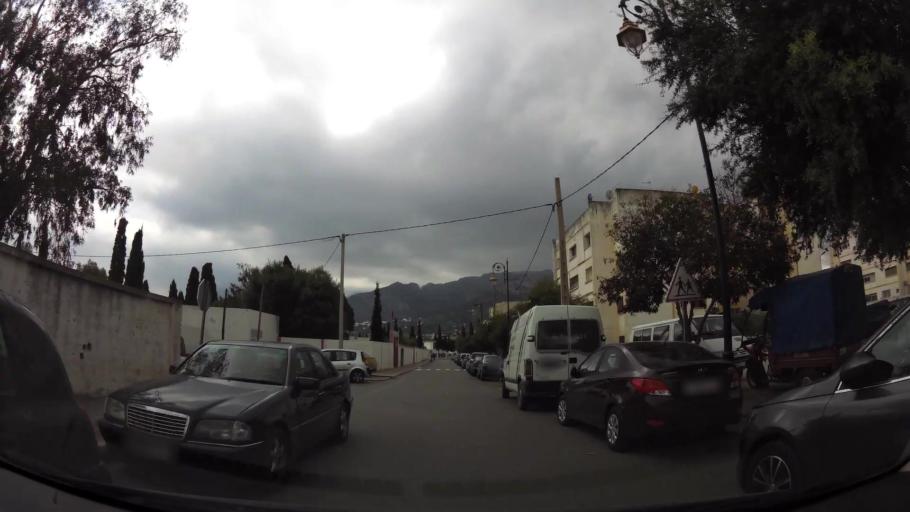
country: MA
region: Tanger-Tetouan
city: Tetouan
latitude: 35.5640
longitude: -5.3636
